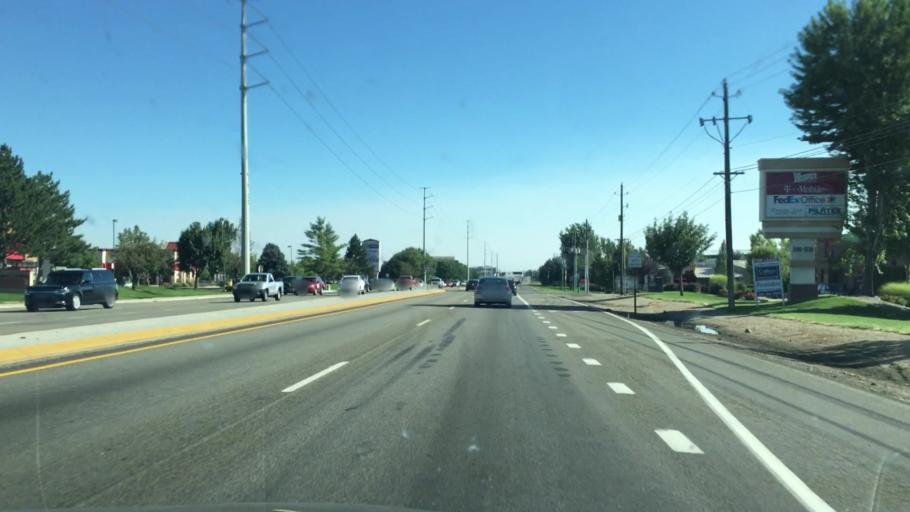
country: US
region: Idaho
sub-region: Ada County
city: Meridian
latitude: 43.6177
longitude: -116.3547
